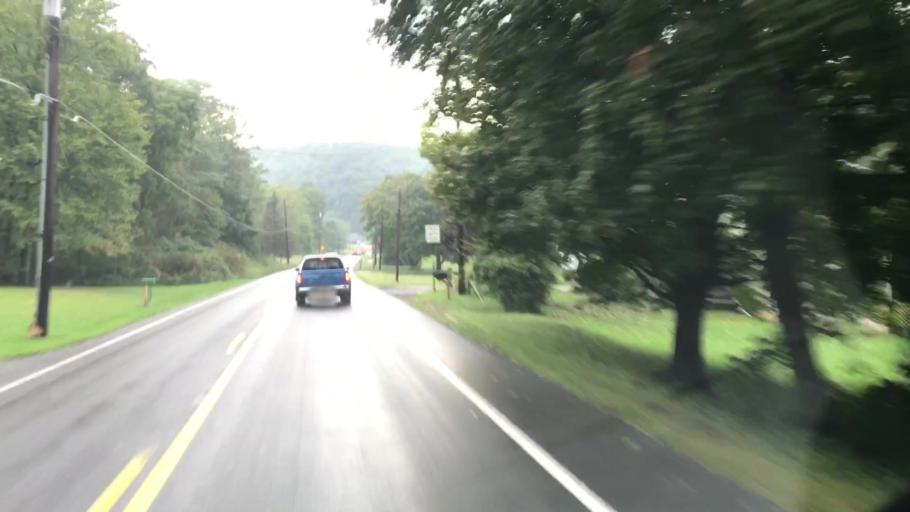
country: US
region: Pennsylvania
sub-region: Cumberland County
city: Schlusser
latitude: 40.3007
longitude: -77.1454
